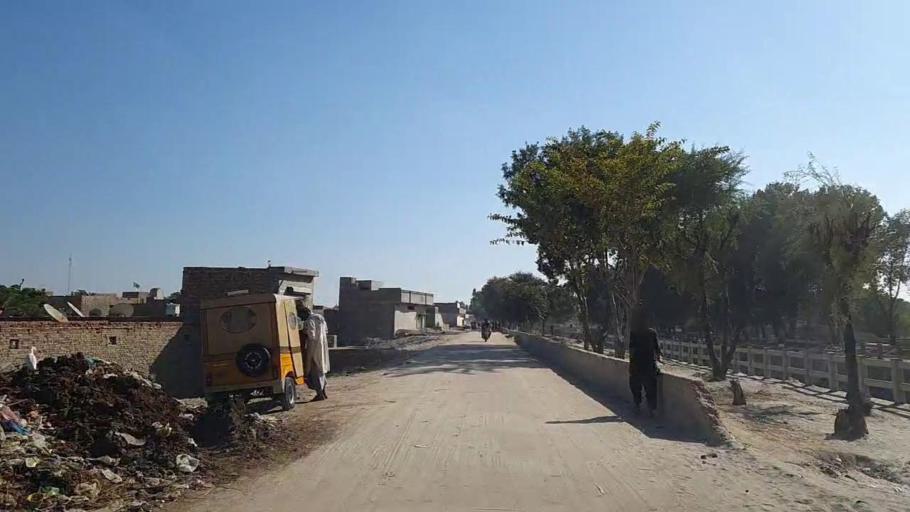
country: PK
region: Sindh
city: Nawabshah
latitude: 26.2565
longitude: 68.4183
